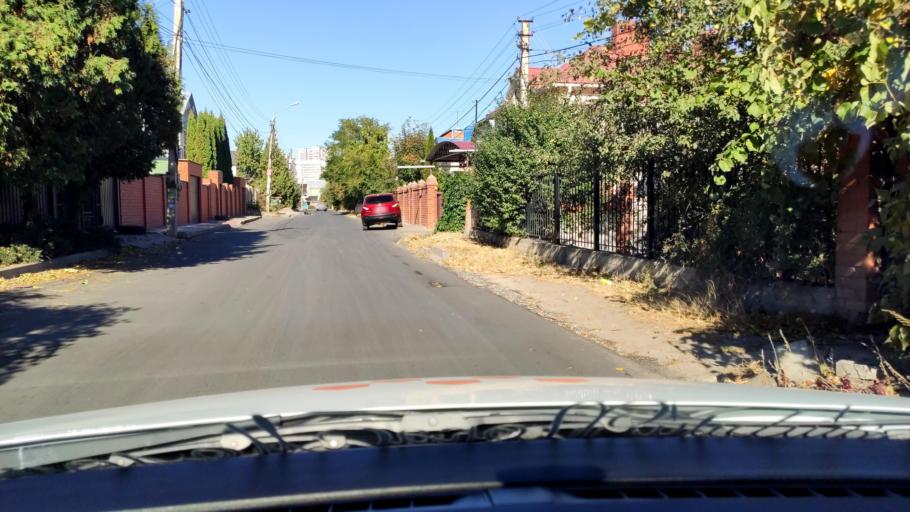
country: RU
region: Voronezj
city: Voronezh
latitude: 51.7035
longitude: 39.2048
